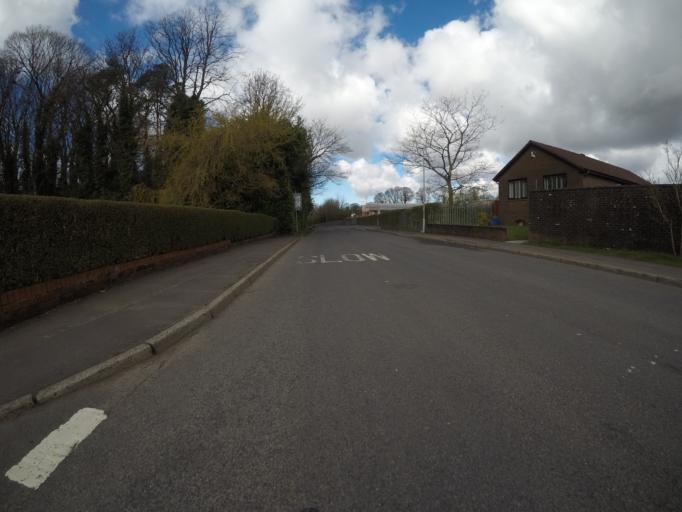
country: GB
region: Scotland
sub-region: North Ayrshire
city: Beith
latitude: 55.7469
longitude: -4.6316
